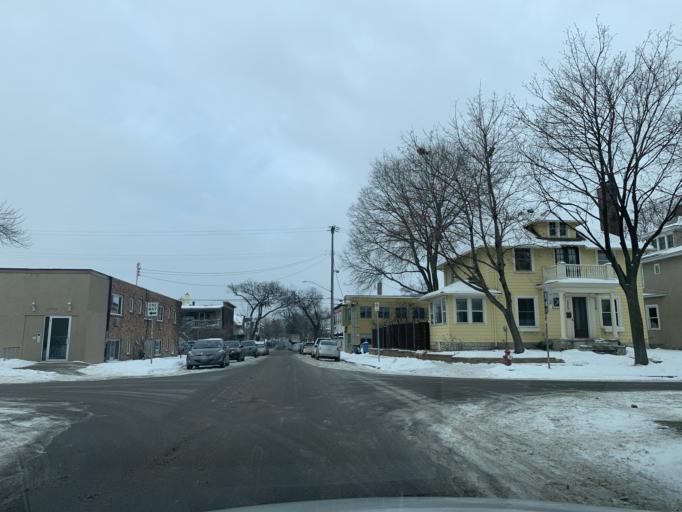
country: US
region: Minnesota
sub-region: Hennepin County
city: Minneapolis
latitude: 44.9538
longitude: -93.2866
